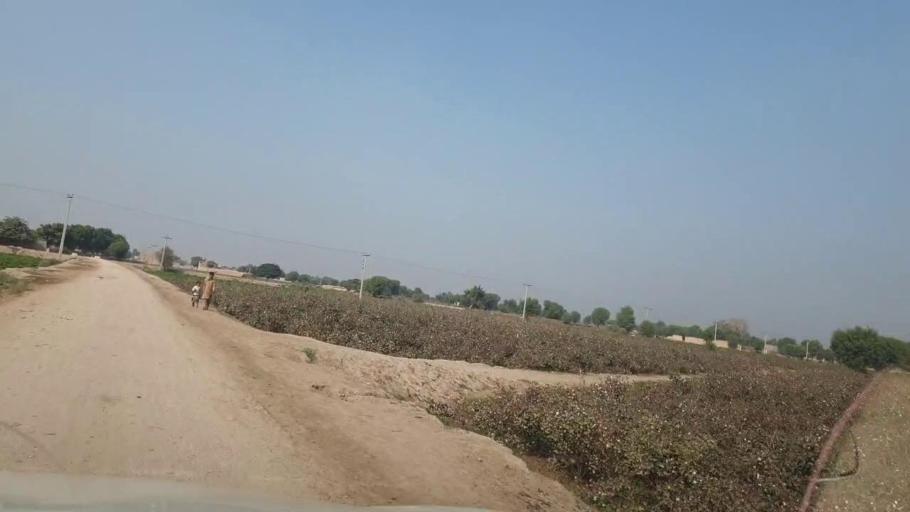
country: PK
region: Sindh
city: Bhan
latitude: 26.5438
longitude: 67.7384
